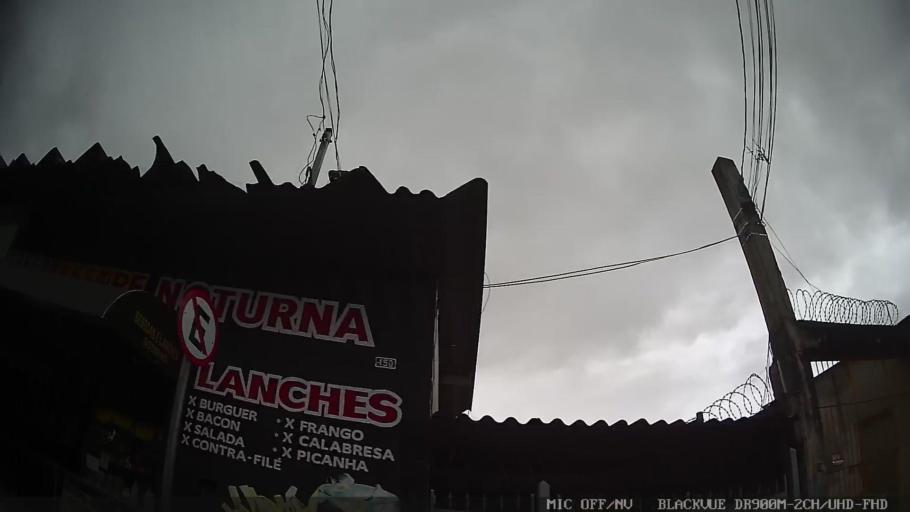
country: BR
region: Sao Paulo
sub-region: Osasco
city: Osasco
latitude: -23.4741
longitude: -46.7142
